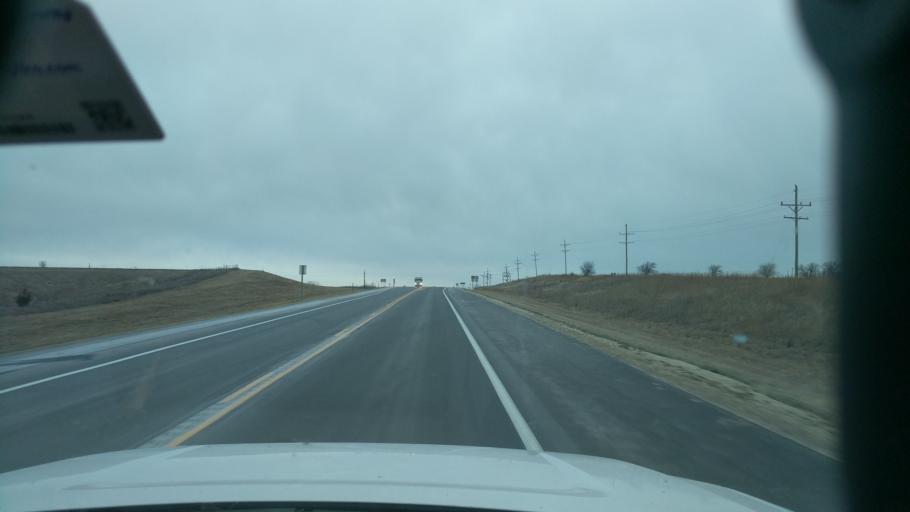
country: US
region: Kansas
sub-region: Marion County
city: Hillsboro
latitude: 38.3625
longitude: -97.3307
